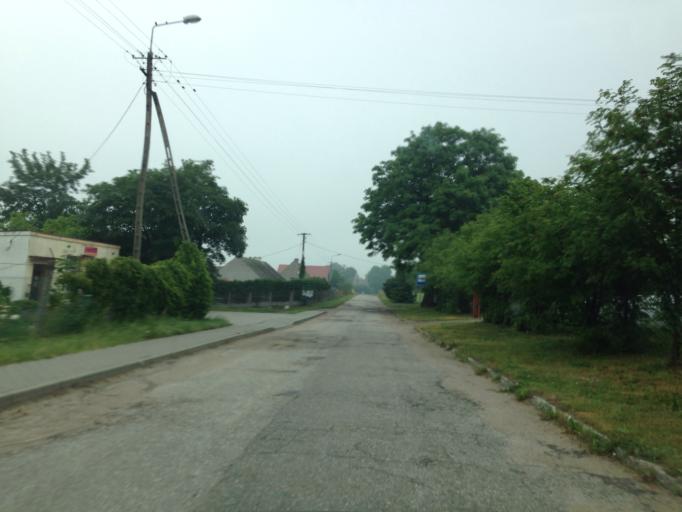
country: PL
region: Kujawsko-Pomorskie
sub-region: Powiat brodnicki
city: Brodnica
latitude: 53.2955
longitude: 19.3425
